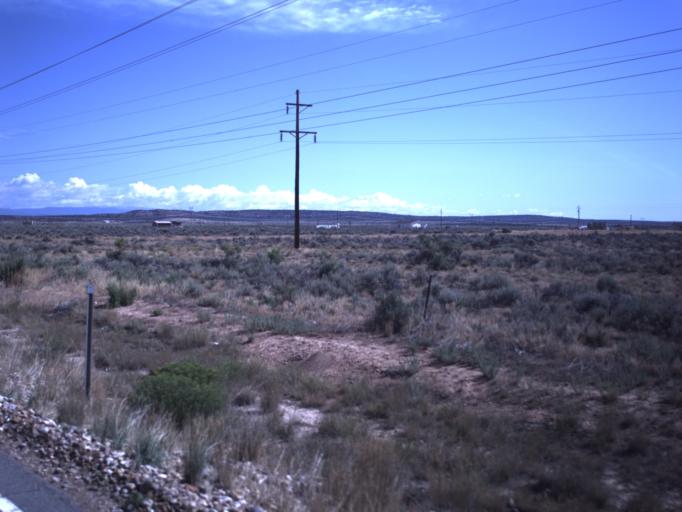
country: US
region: Utah
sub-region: Duchesne County
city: Duchesne
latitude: 40.2287
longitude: -110.3893
